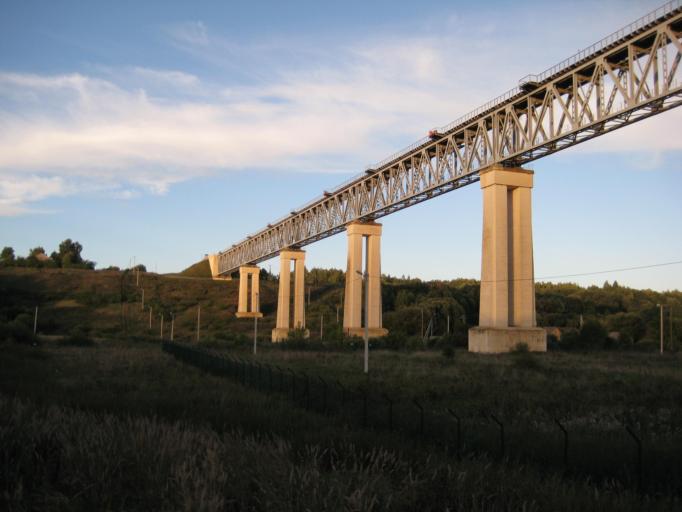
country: LT
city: Raseiniai
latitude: 55.5061
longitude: 23.0843
